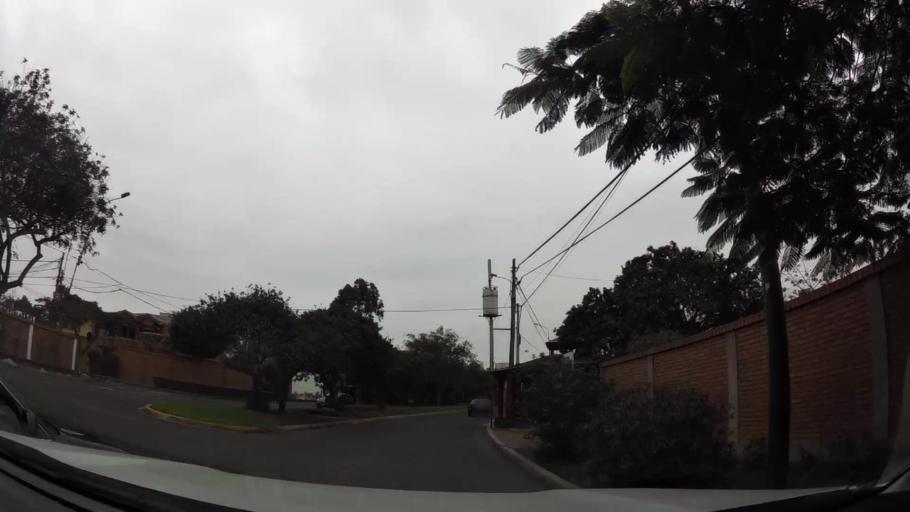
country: PE
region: Lima
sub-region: Lima
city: La Molina
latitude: -12.1087
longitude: -76.9631
